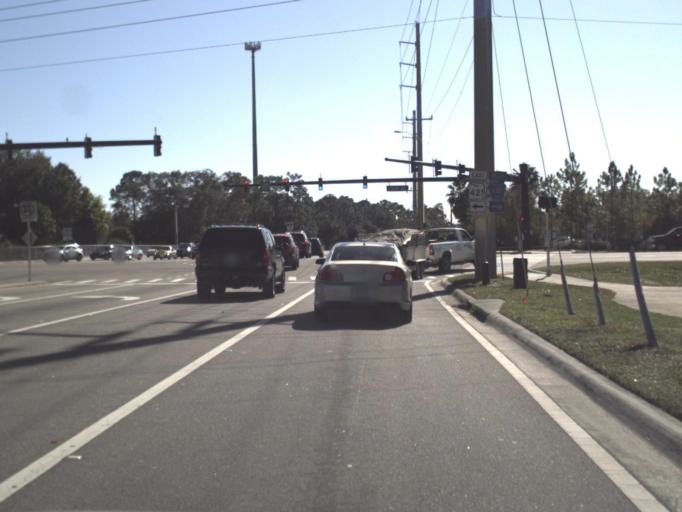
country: US
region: Florida
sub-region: Volusia County
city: Port Orange
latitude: 29.1054
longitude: -81.0319
